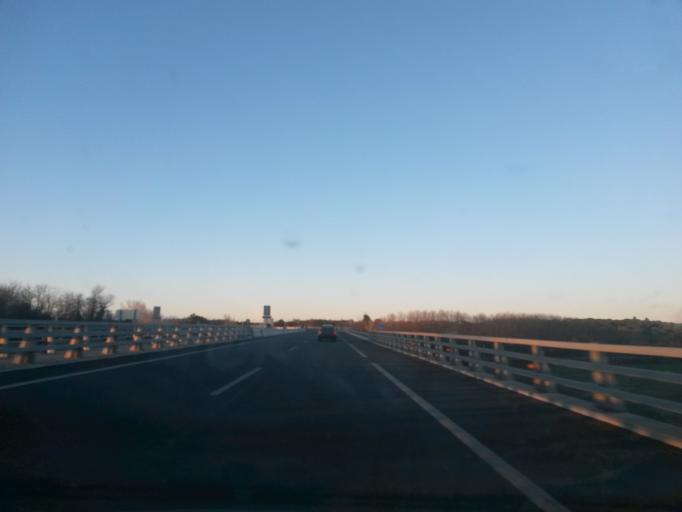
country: ES
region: Catalonia
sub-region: Provincia de Girona
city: Sils
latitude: 41.8150
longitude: 2.7641
